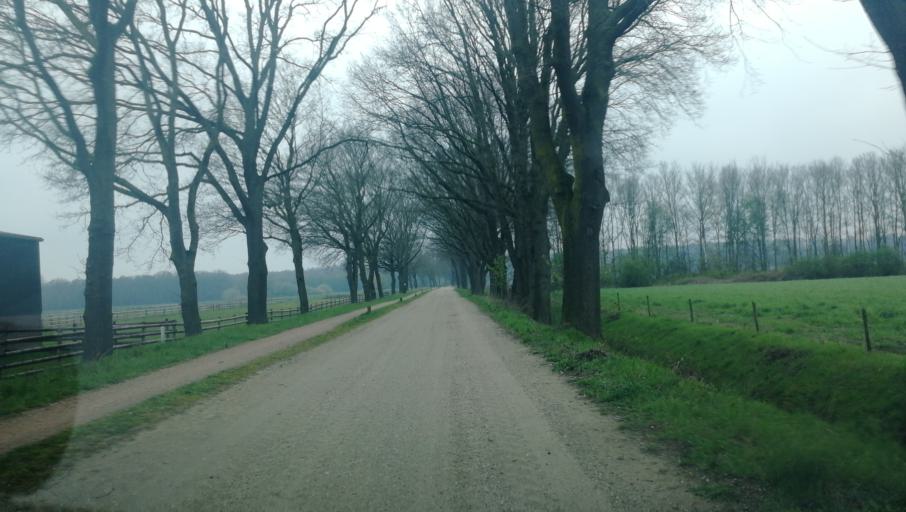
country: NL
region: Limburg
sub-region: Gemeente Beesel
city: Beesel
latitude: 51.2894
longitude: 6.0084
